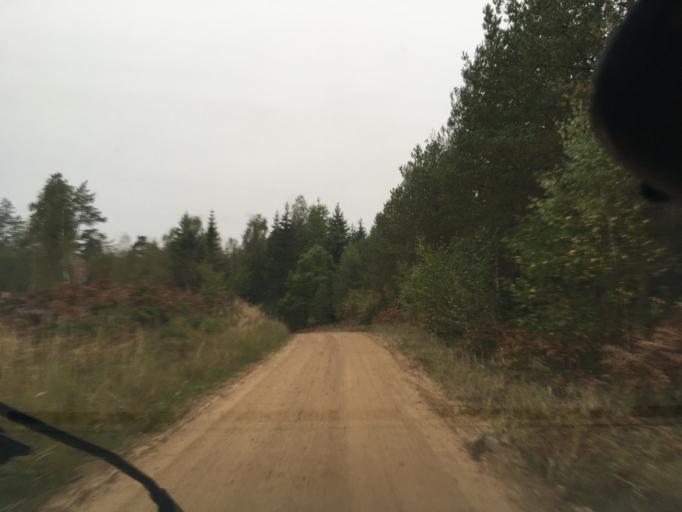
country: LV
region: Kuldigas Rajons
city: Kuldiga
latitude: 57.0228
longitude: 21.9976
